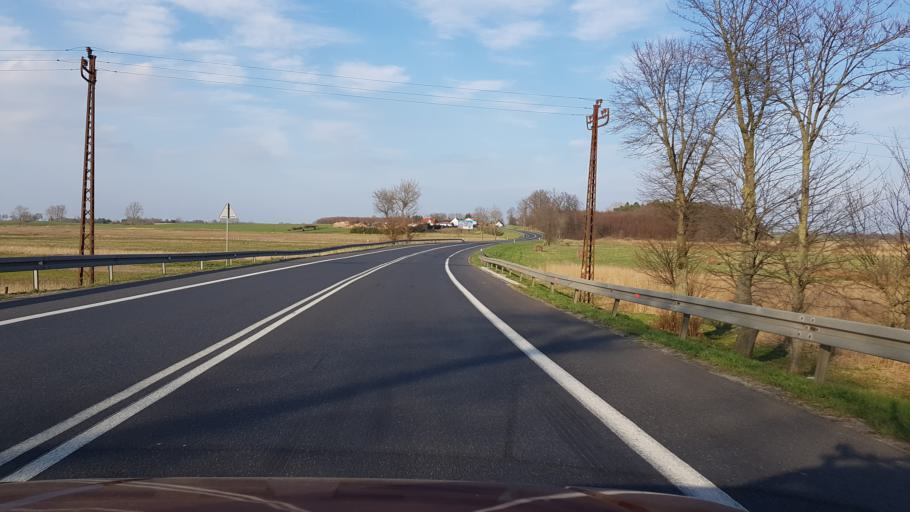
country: PL
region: West Pomeranian Voivodeship
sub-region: Powiat bialogardzki
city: Bialogard
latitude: 54.1218
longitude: 16.0106
